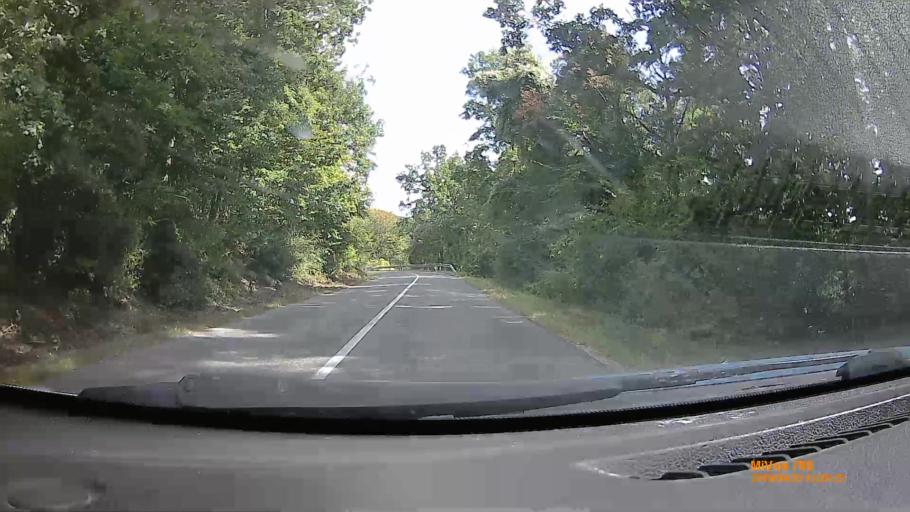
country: HU
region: Heves
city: Szilvasvarad
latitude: 48.0441
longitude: 20.4820
